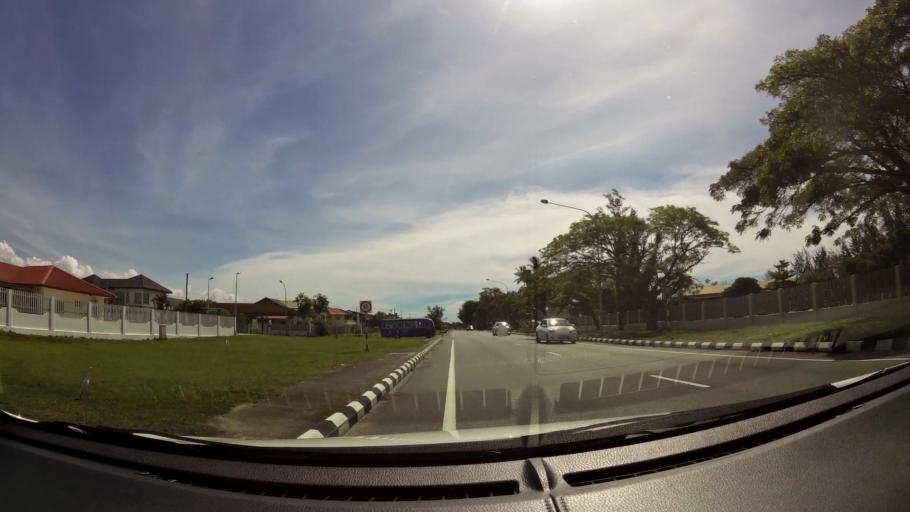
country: BN
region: Belait
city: Kuala Belait
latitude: 4.5892
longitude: 114.2072
